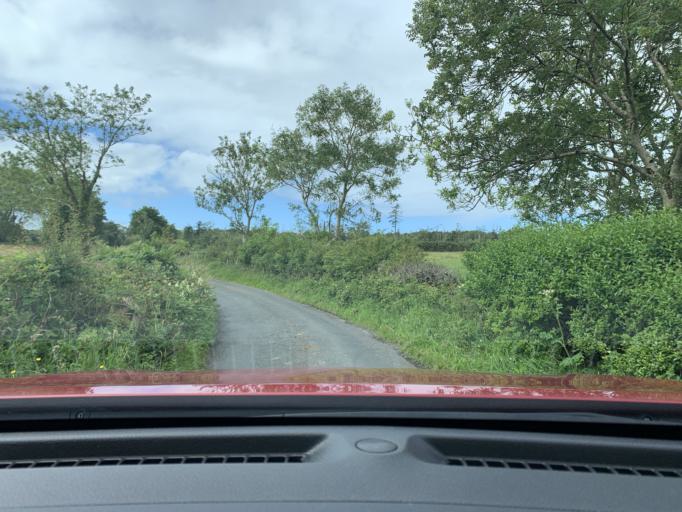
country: IE
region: Connaught
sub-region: Sligo
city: Sligo
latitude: 54.3809
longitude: -8.5231
